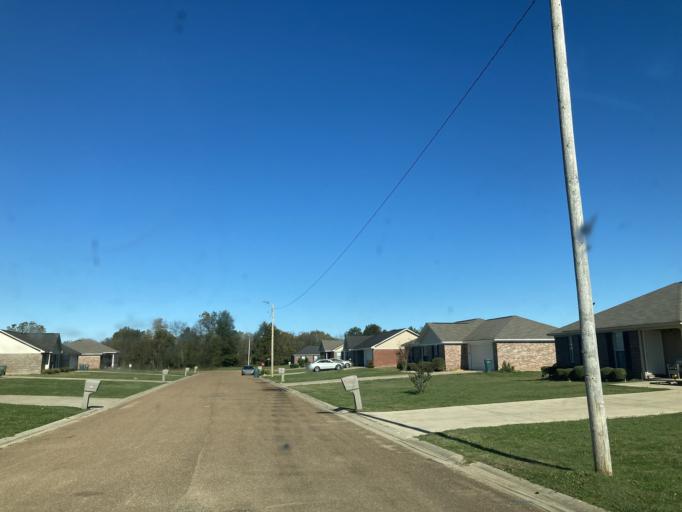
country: US
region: Mississippi
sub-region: Yazoo County
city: Yazoo City
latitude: 32.8580
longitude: -90.4270
